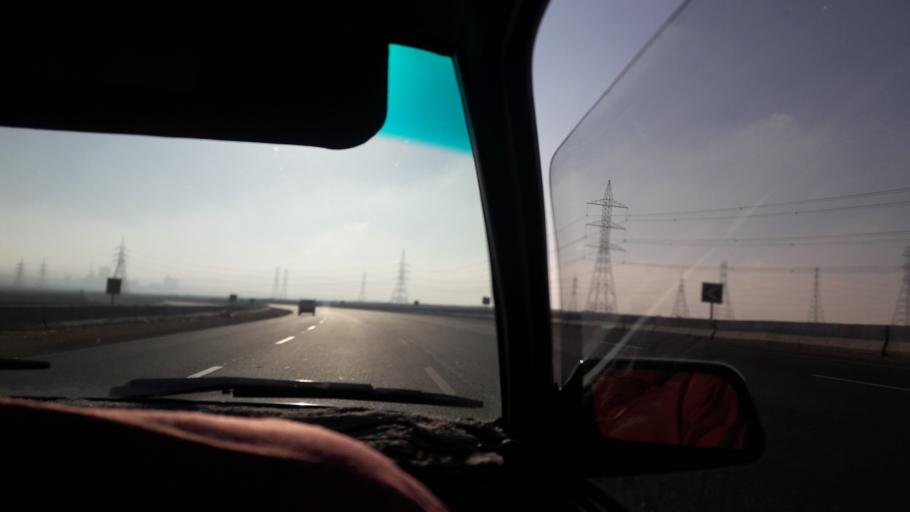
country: EG
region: Muhafazat al Qahirah
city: Halwan
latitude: 29.9041
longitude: 31.4982
